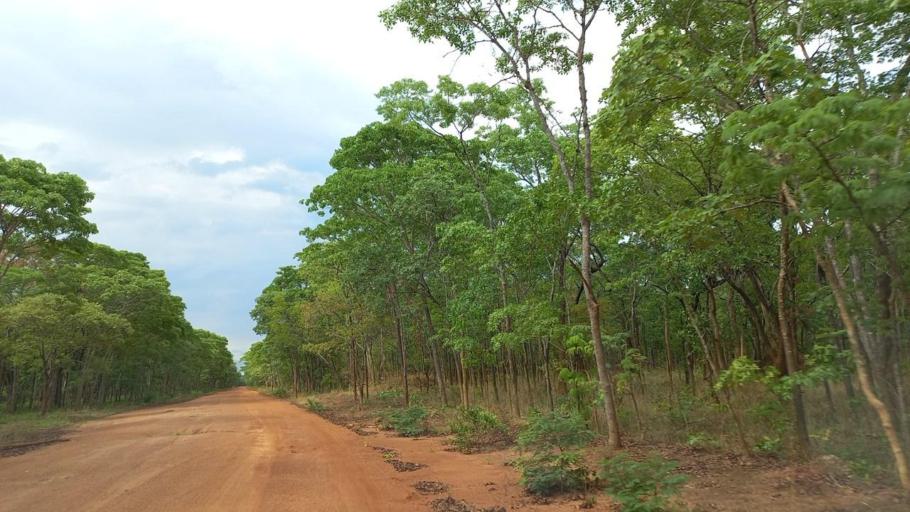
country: ZM
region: North-Western
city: Kalengwa
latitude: -13.4036
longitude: 25.0653
